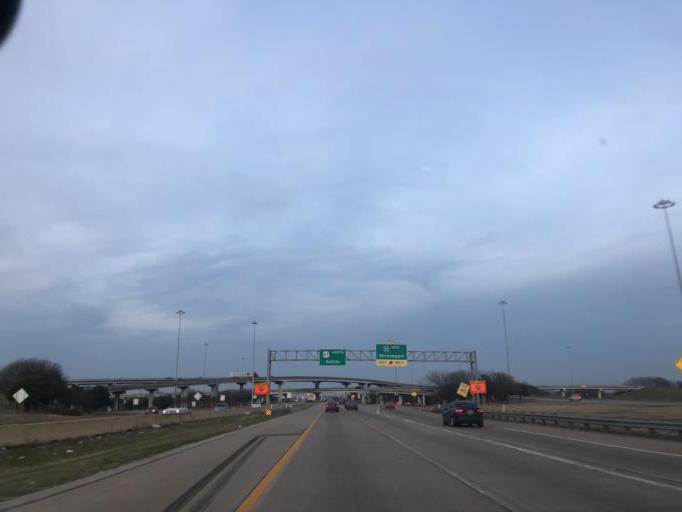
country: US
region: Texas
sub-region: Dallas County
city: Duncanville
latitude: 32.6516
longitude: -96.8804
